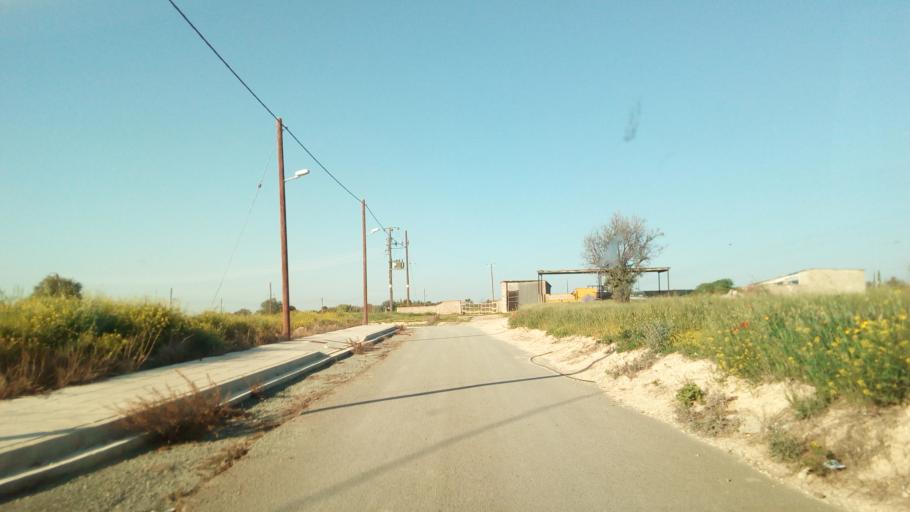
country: CY
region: Larnaka
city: Kofinou
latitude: 34.8460
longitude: 33.4583
